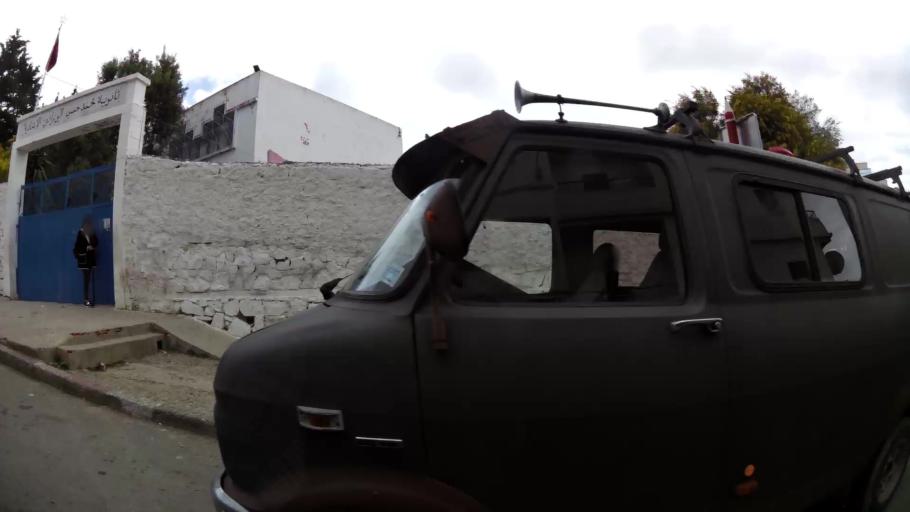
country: MA
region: Tanger-Tetouan
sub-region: Tanger-Assilah
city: Tangier
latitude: 35.7727
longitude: -5.8195
